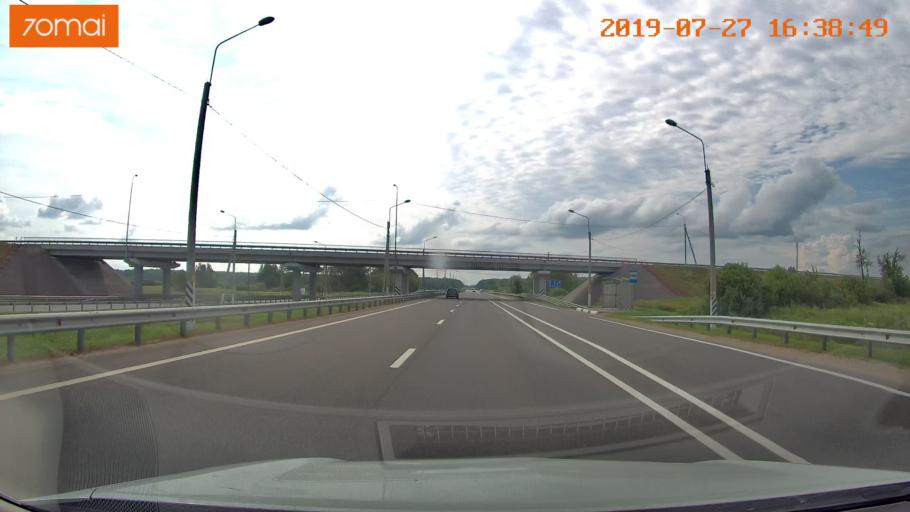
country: RU
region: Kaliningrad
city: Gvardeysk
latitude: 54.6491
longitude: 21.2179
